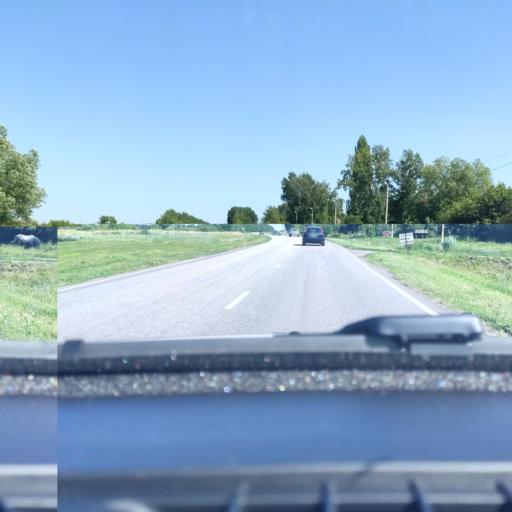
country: RU
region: Voronezj
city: Verkhnyaya Khava
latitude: 51.6690
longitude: 39.9603
